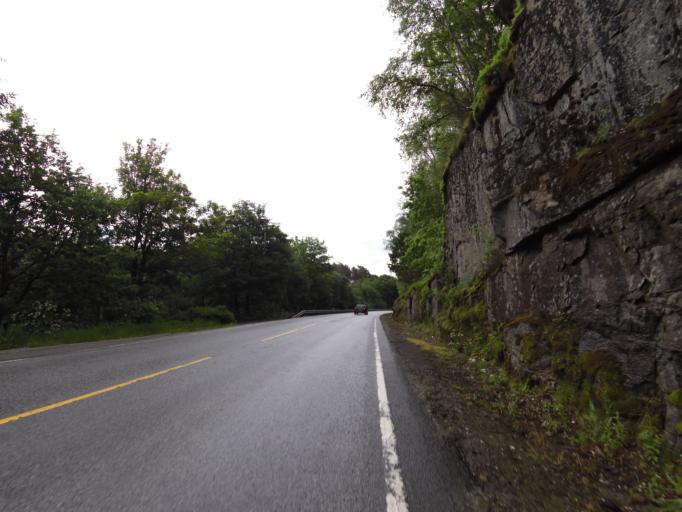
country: NO
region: Vest-Agder
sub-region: Farsund
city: Farsund
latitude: 58.1023
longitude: 6.8531
